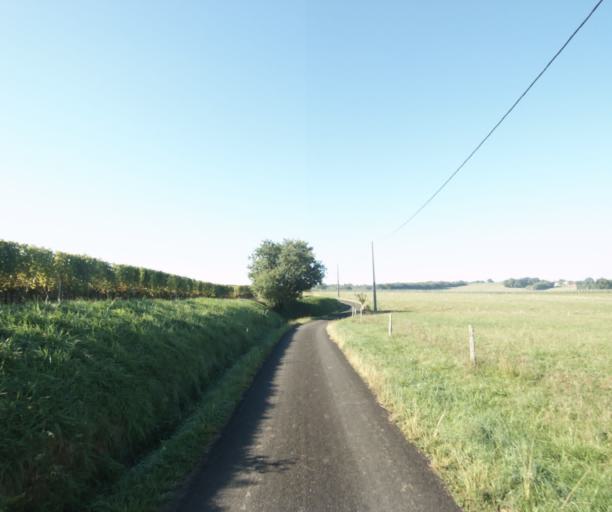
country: FR
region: Midi-Pyrenees
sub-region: Departement du Gers
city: Vic-Fezensac
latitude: 43.8241
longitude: 0.2765
